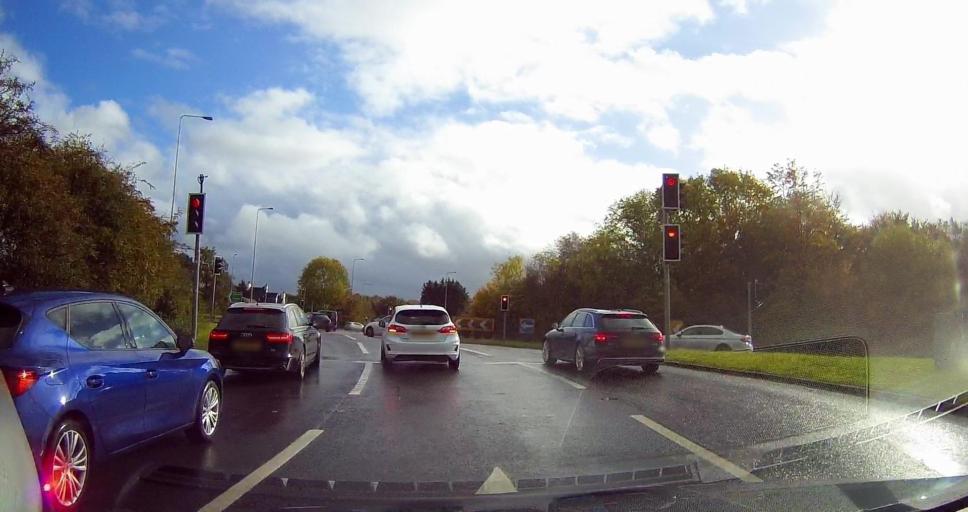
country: GB
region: England
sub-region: City and Borough of Birmingham
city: Sutton Coldfield
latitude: 52.5915
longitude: -1.7839
